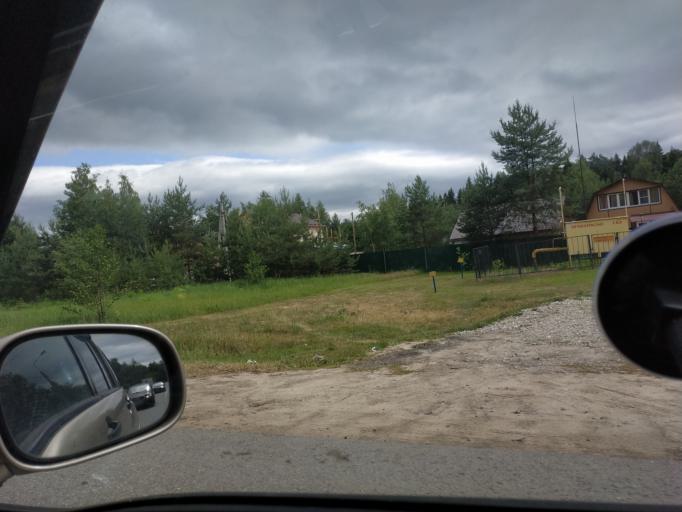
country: RU
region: Moskovskaya
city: Krasnoarmeysk
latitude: 56.0184
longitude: 38.1613
